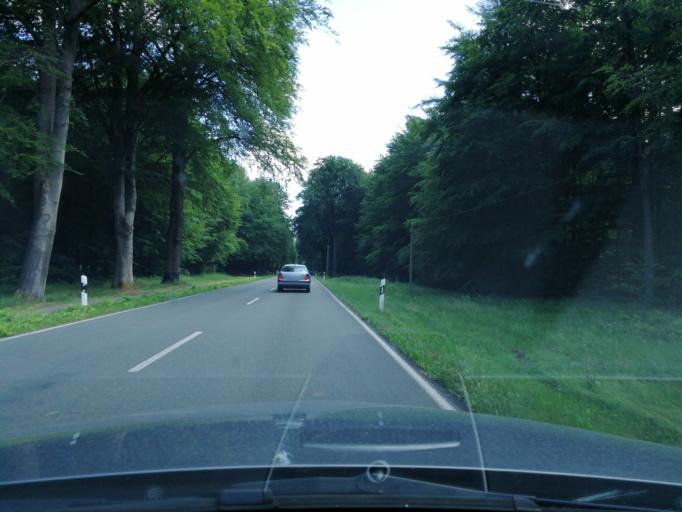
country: DE
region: North Rhine-Westphalia
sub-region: Regierungsbezirk Dusseldorf
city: Kranenburg
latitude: 51.7346
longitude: 6.0736
